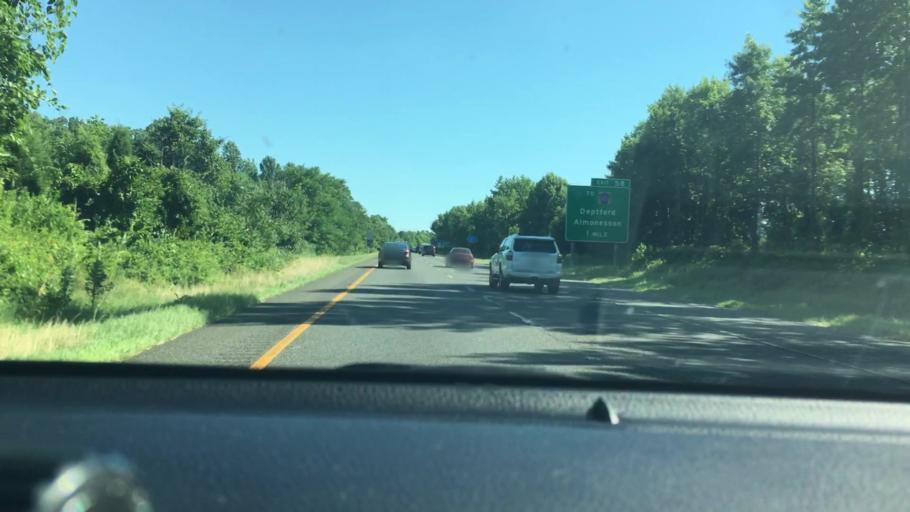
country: US
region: New Jersey
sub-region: Camden County
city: Bellmawr
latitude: 39.8435
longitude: -75.0976
